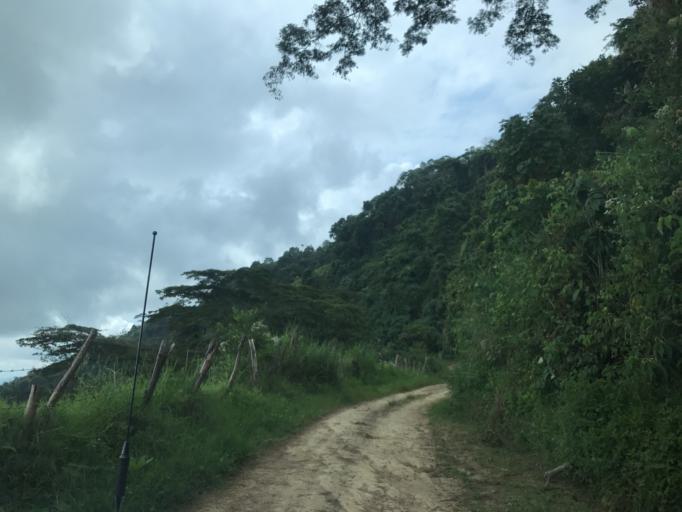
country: CO
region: Valle del Cauca
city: Obando
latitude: 4.5649
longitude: -75.8936
